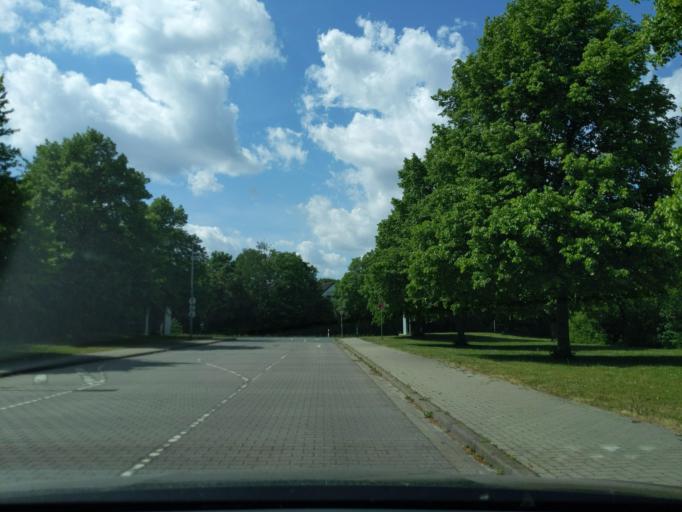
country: DE
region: Lower Saxony
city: Laatzen
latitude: 52.3349
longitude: 9.8228
